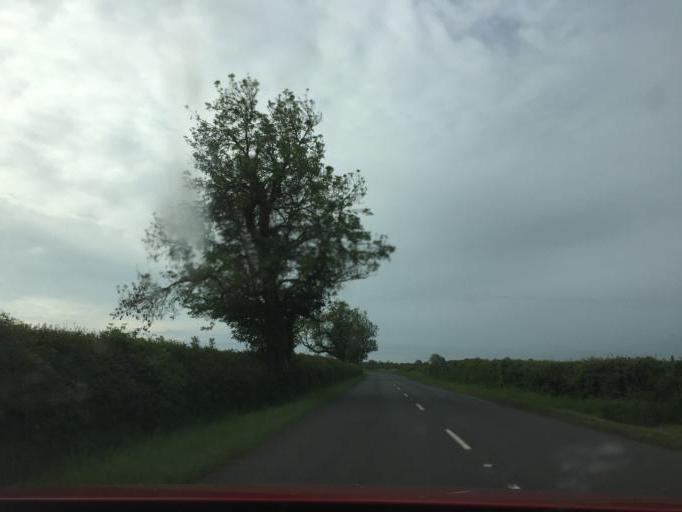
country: GB
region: England
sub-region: Leicestershire
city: Hinckley
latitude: 52.4895
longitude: -1.3474
